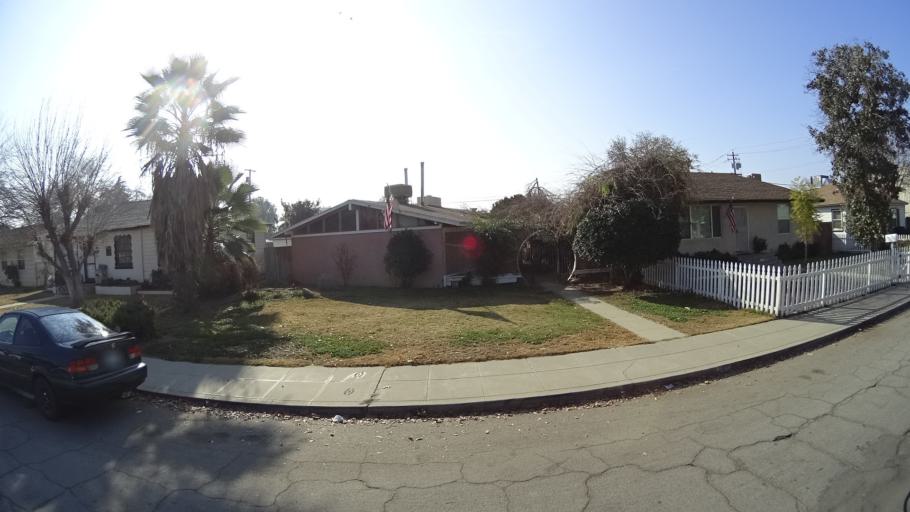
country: US
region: California
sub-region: Kern County
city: Bakersfield
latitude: 35.3858
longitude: -119.0016
